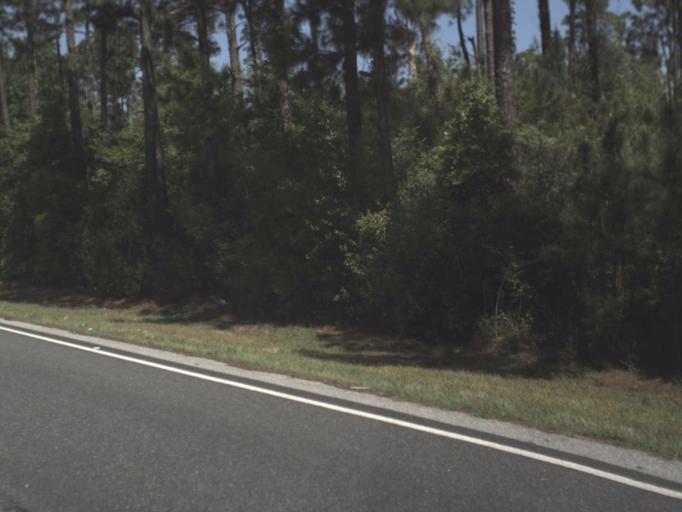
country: US
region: Florida
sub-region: Escambia County
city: Ensley
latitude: 30.5232
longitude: -87.3166
